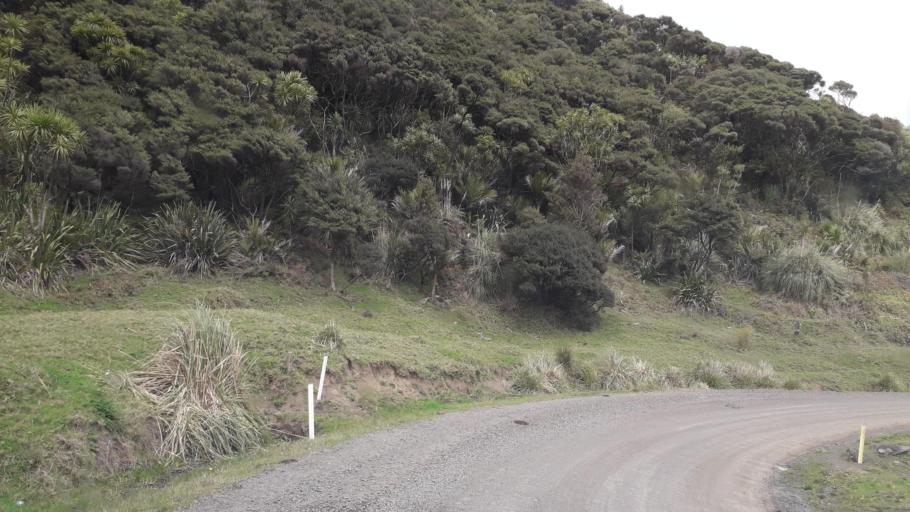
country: NZ
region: Northland
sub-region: Far North District
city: Ahipara
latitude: -35.4375
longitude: 173.3061
